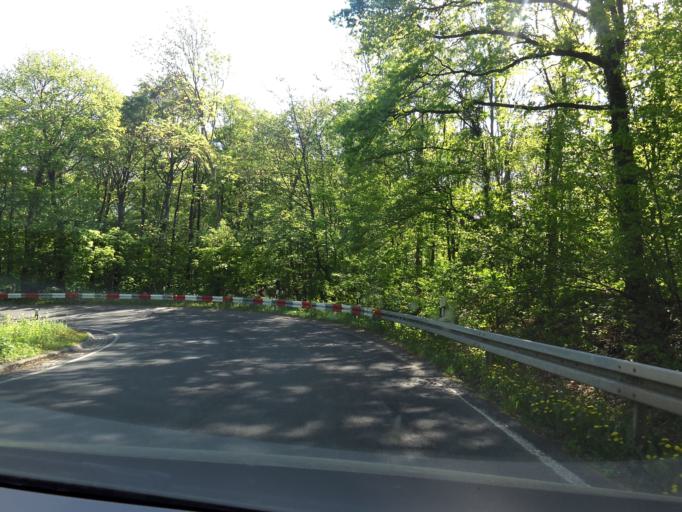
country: DE
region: Thuringia
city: Gierstadt
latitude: 51.0328
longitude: 10.8350
